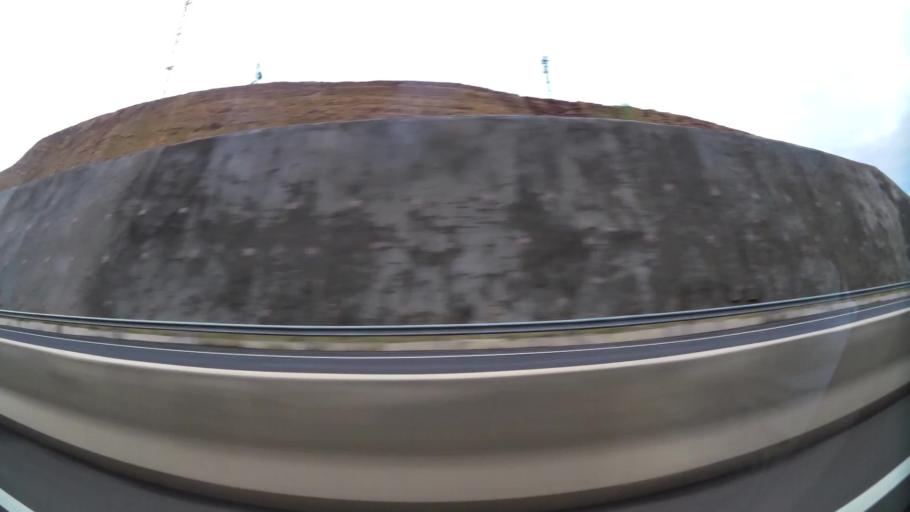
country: MA
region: Oriental
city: Taourirt
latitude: 34.4665
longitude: -3.0176
